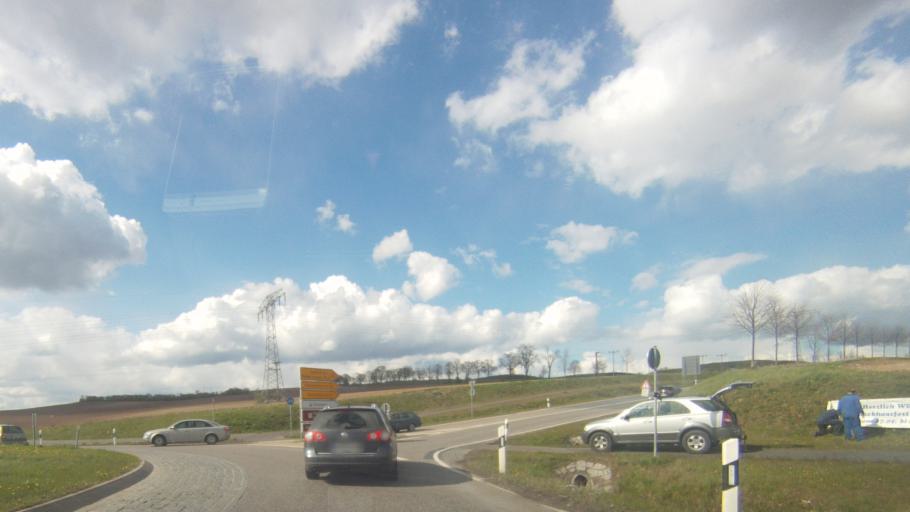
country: DE
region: Thuringia
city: Eisfeld
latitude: 50.4323
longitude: 10.8972
